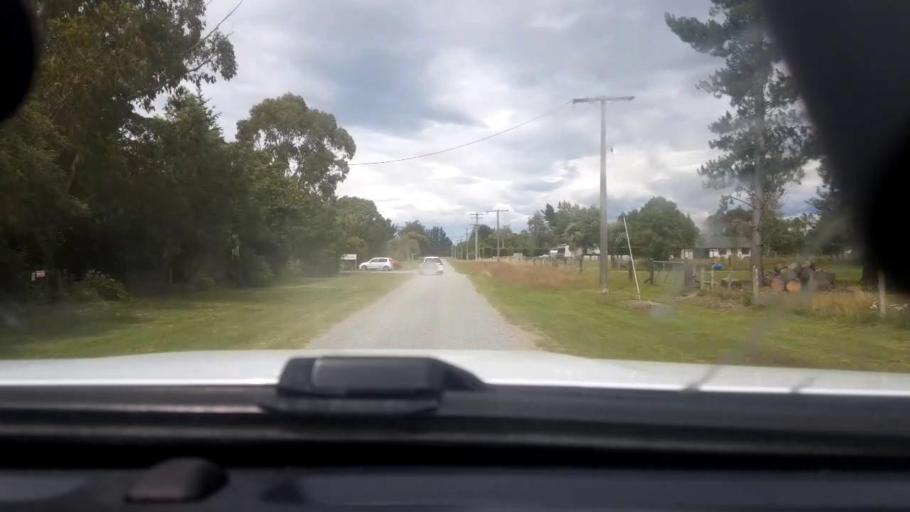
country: NZ
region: Canterbury
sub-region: Timaru District
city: Pleasant Point
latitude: -44.1404
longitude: 171.2906
